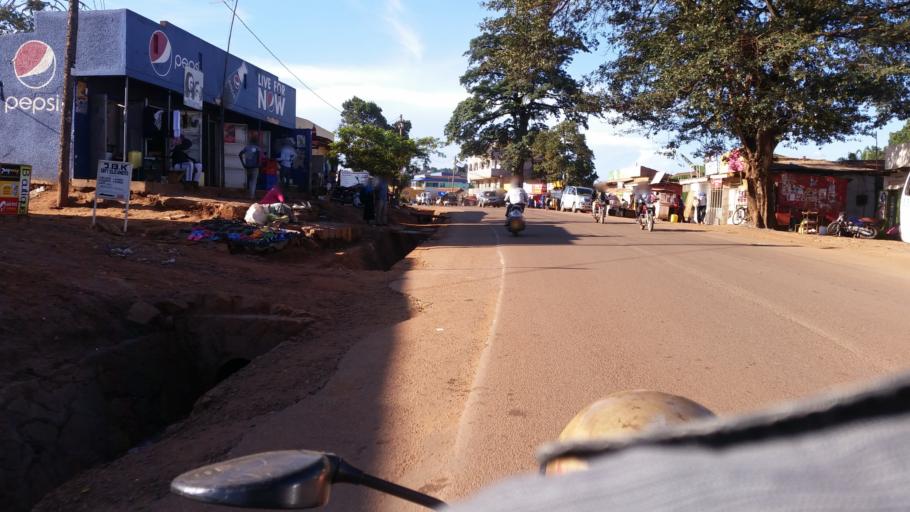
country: UG
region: Central Region
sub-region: Wakiso District
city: Kireka
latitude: 0.3221
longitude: 32.6362
